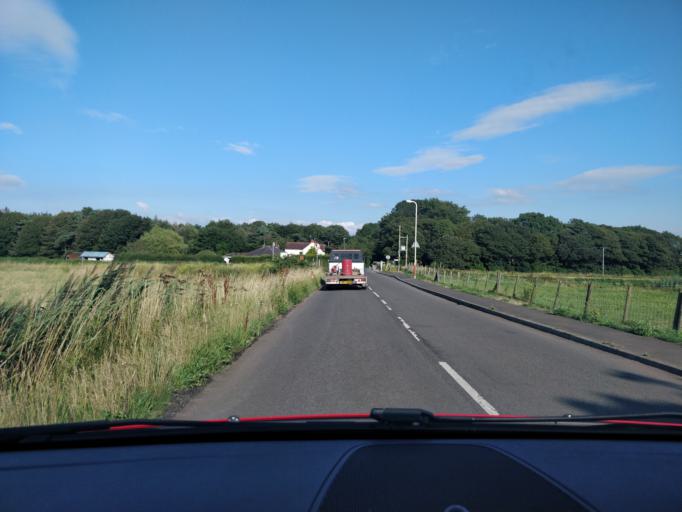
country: GB
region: England
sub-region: Lancashire
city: Banks
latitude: 53.6525
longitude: -2.9510
